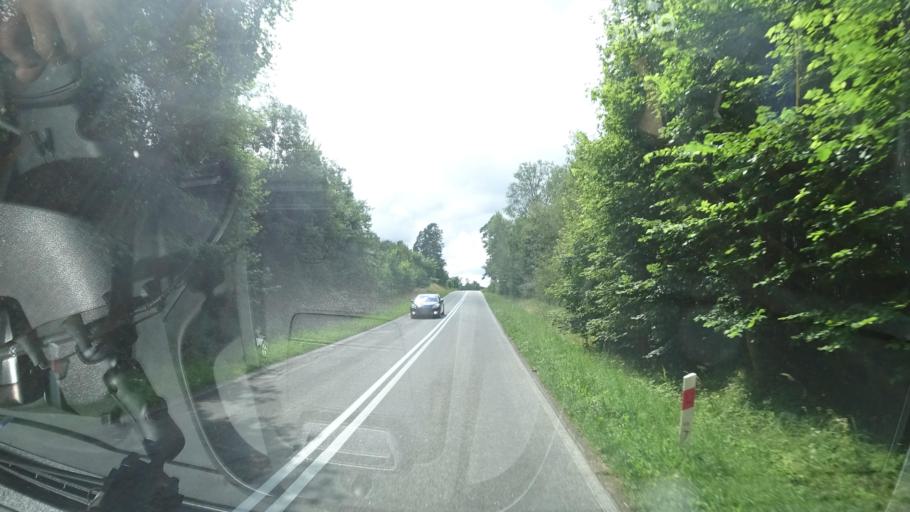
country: PL
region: Warmian-Masurian Voivodeship
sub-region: Powiat goldapski
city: Goldap
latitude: 54.2103
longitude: 22.2034
